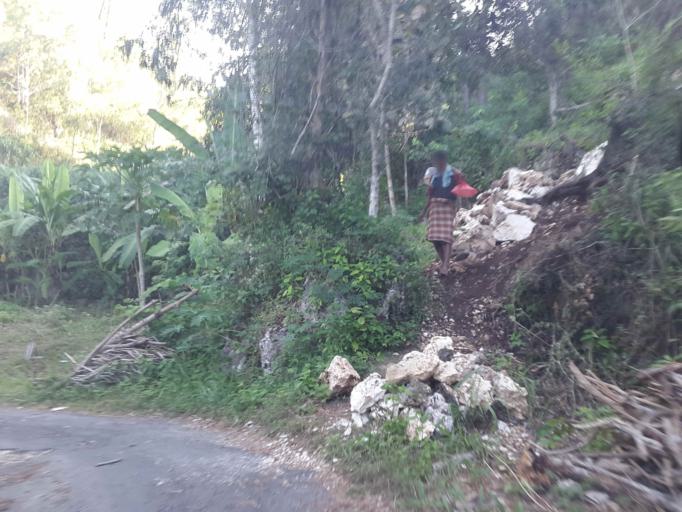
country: ID
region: Bali
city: Gelagah
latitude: -8.7216
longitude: 115.5649
